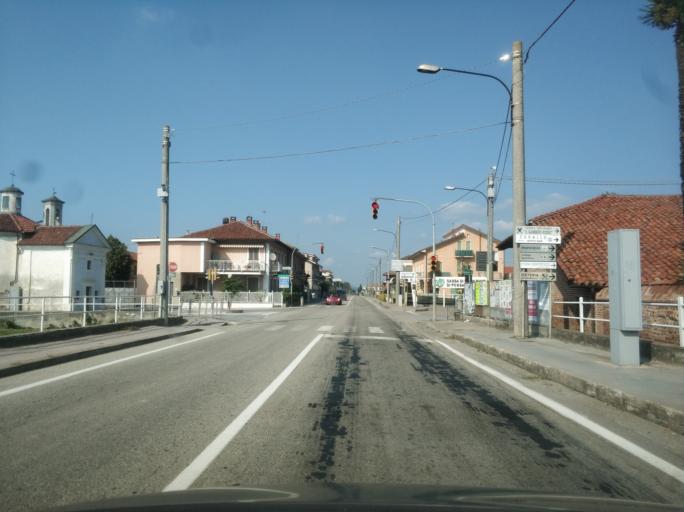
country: IT
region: Piedmont
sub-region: Provincia di Cuneo
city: Cervere
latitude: 44.6358
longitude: 7.7892
